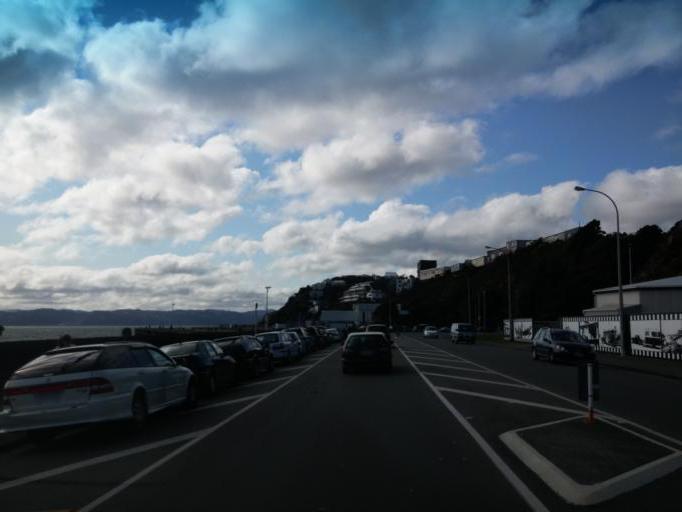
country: NZ
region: Wellington
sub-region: Wellington City
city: Wellington
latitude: -41.3154
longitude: 174.8103
